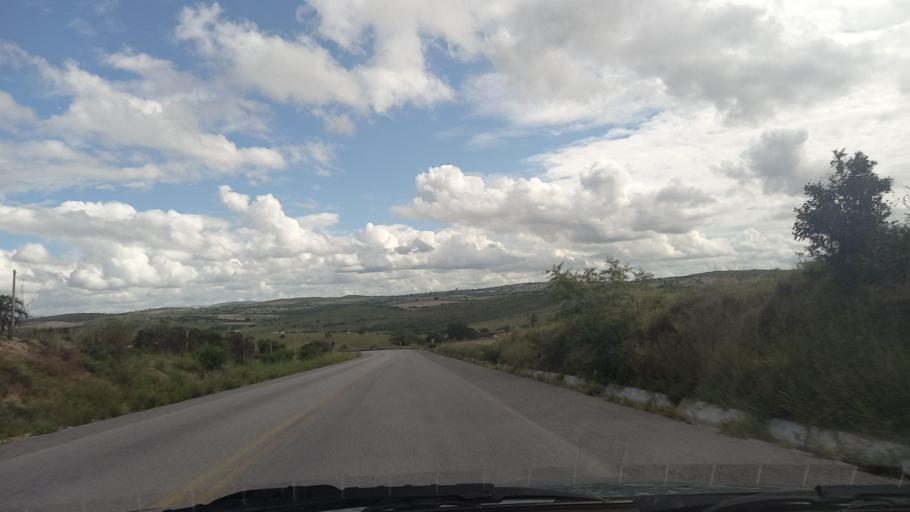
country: BR
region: Pernambuco
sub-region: Lajedo
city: Lajedo
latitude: -8.7256
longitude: -36.4301
